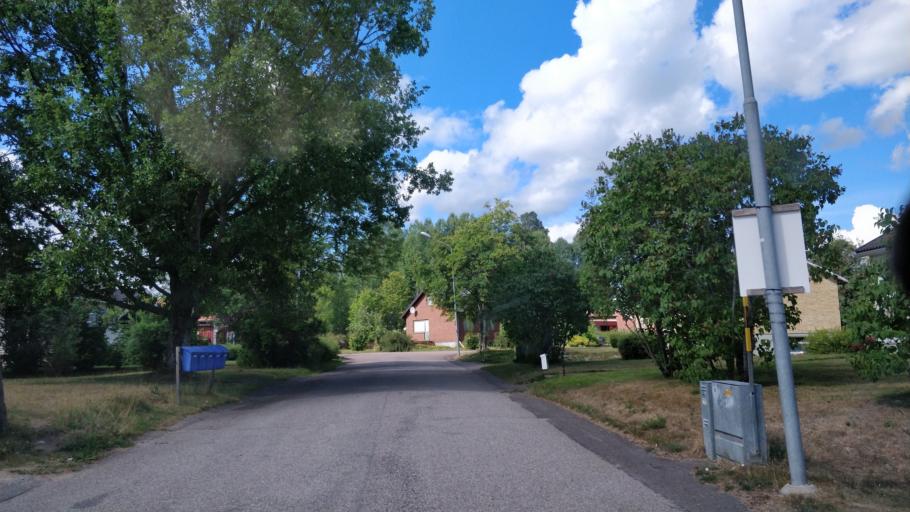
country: SE
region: Vaermland
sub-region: Hagfors Kommun
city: Hagfors
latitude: 60.0437
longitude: 13.6749
